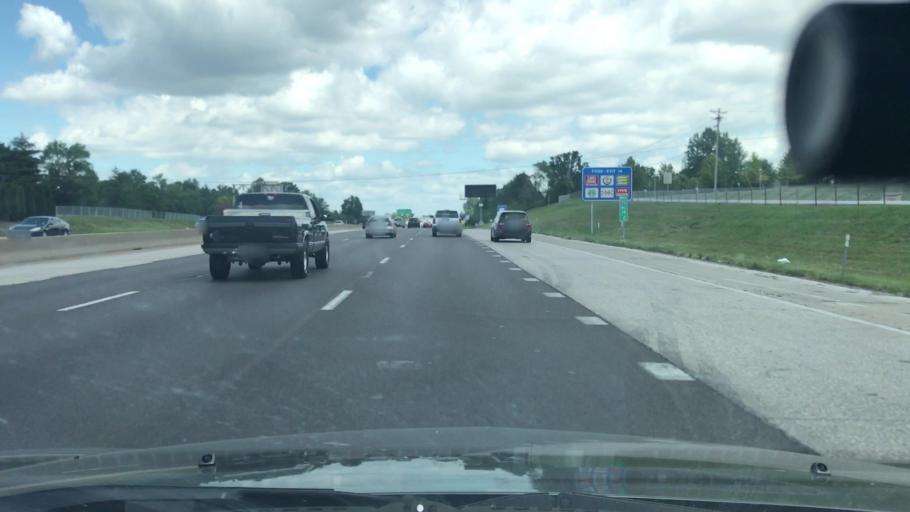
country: US
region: Missouri
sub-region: Saint Louis County
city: Creve Coeur
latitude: 38.6602
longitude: -90.4483
